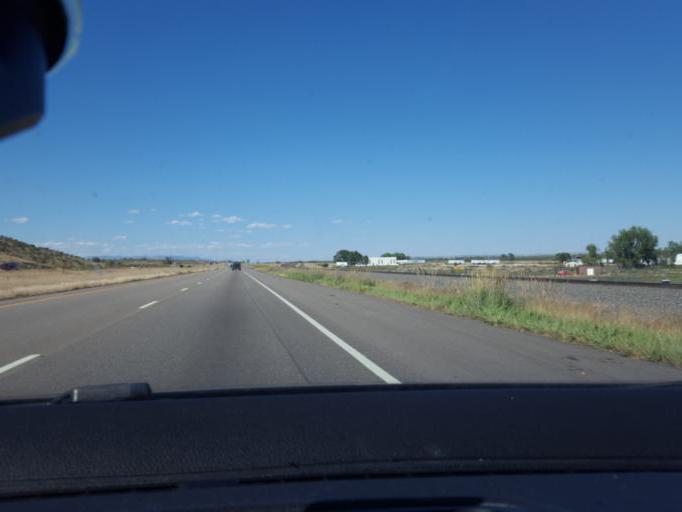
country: US
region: Colorado
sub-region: El Paso County
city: Fountain
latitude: 38.5391
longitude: -104.6408
